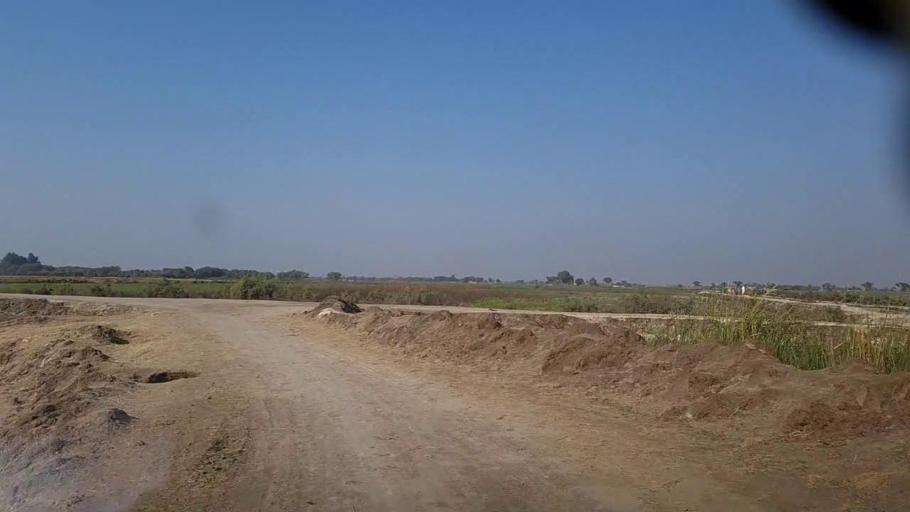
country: PK
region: Sindh
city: Jacobabad
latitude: 28.3111
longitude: 68.5620
